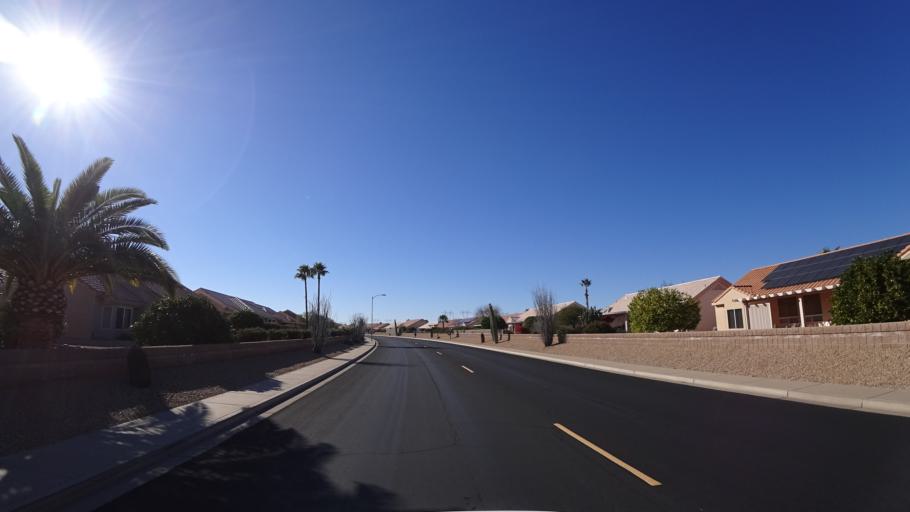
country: US
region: Arizona
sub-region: Maricopa County
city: Sun City West
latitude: 33.6940
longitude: -112.3729
